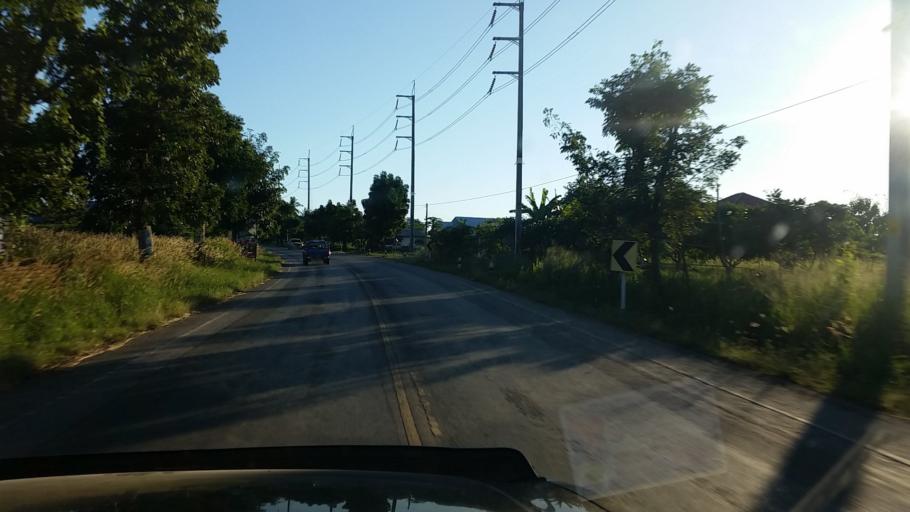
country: TH
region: Chaiyaphum
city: Nong Bua Rawe
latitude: 15.7130
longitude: 101.7391
